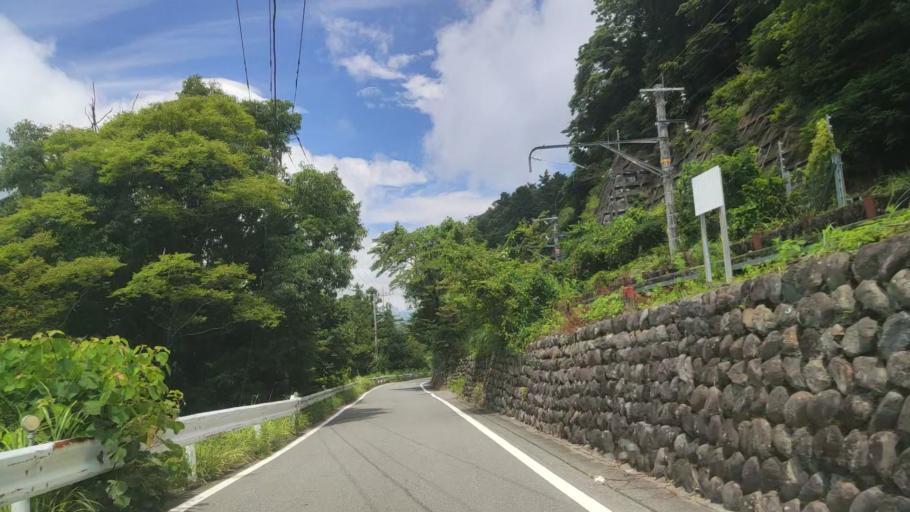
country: JP
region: Shizuoka
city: Fujinomiya
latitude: 35.2480
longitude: 138.4897
